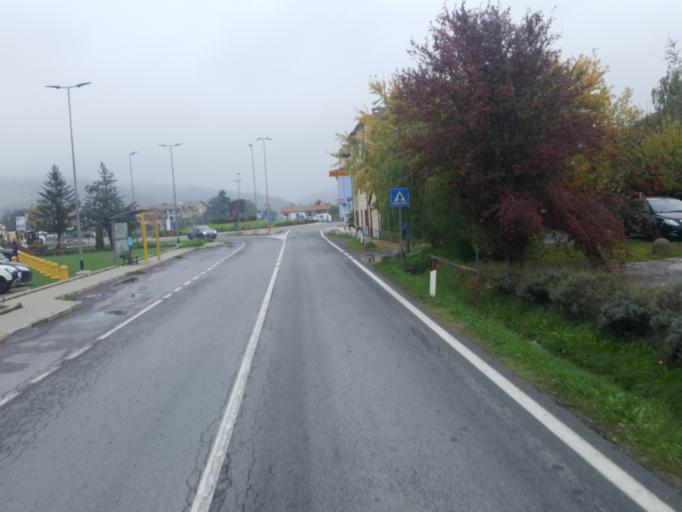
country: IT
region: Piedmont
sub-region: Provincia di Cuneo
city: Ceva
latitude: 44.3763
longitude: 8.0410
